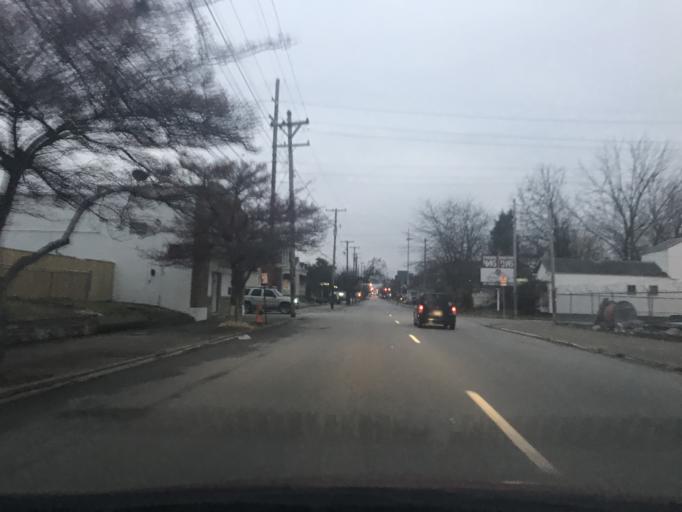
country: US
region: Kentucky
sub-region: Jefferson County
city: Louisville
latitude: 38.2397
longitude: -85.7485
